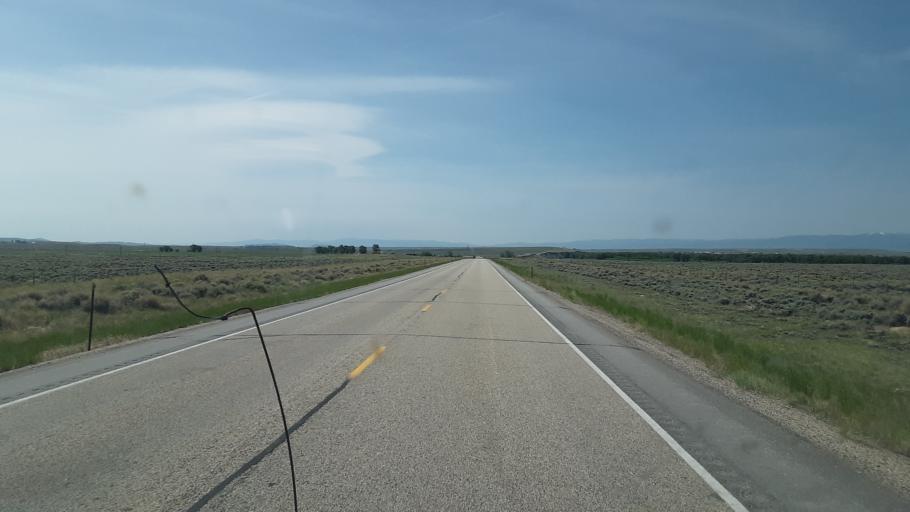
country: US
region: Wyoming
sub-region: Carbon County
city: Saratoga
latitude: 41.5098
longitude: -106.8061
